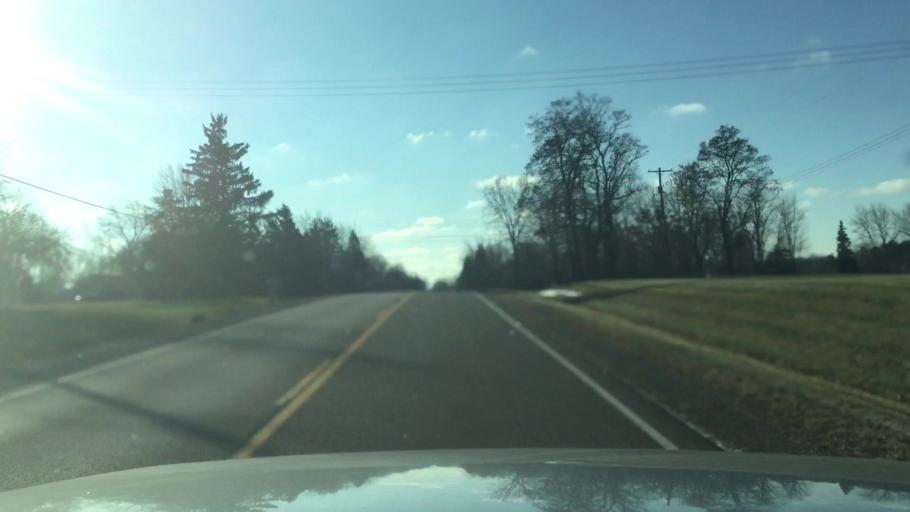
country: US
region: Michigan
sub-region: Genesee County
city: Grand Blanc
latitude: 42.9315
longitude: -83.6620
